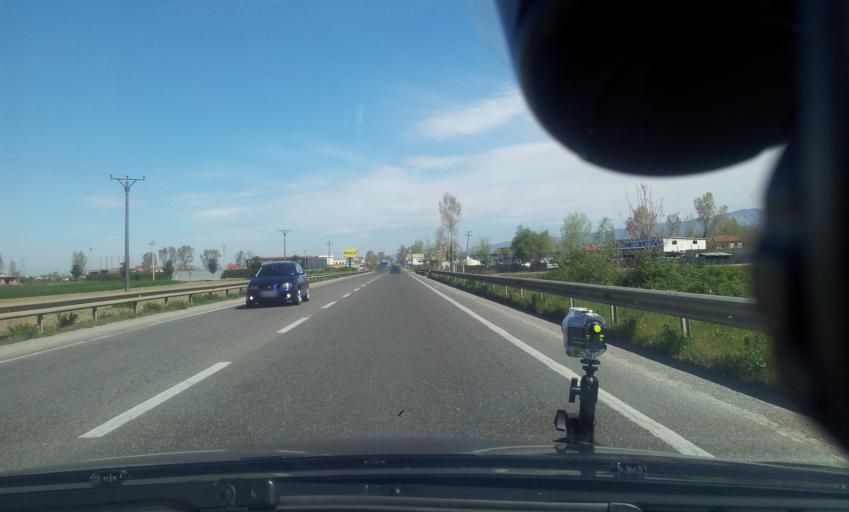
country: AL
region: Tirane
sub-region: Rrethi i Tiranes
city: Preze
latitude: 41.4529
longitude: 19.6890
